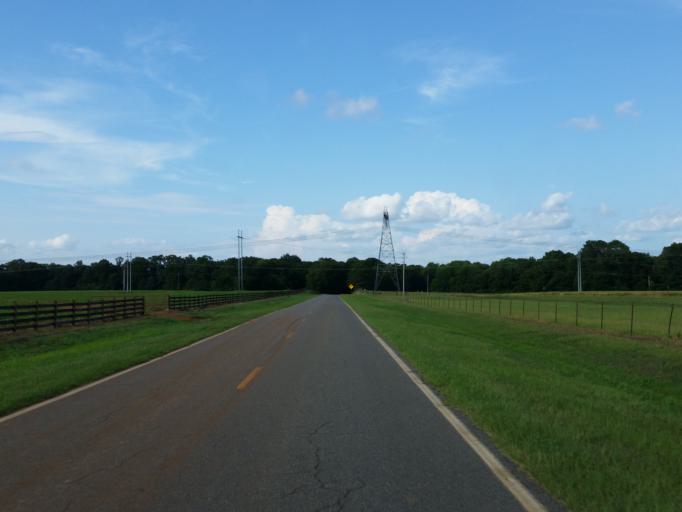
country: US
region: Georgia
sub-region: Lee County
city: Leesburg
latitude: 31.9001
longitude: -84.0439
